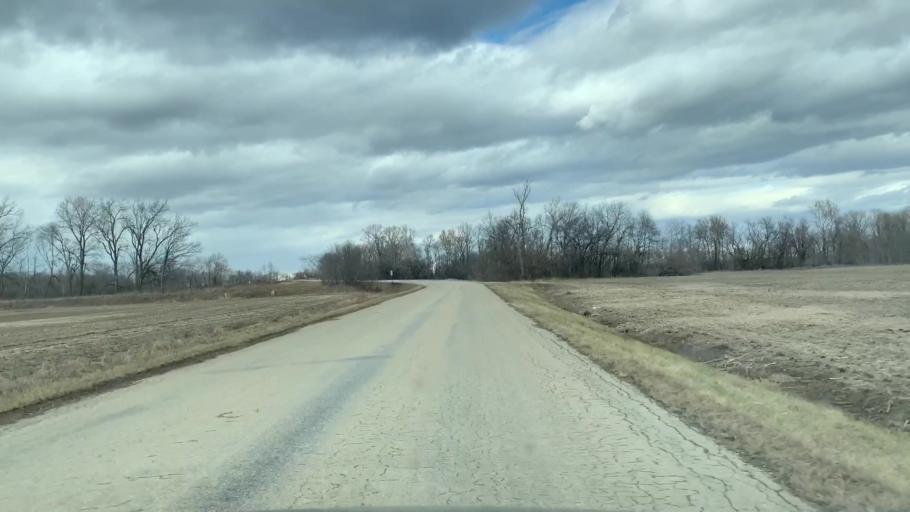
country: US
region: Kansas
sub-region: Allen County
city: Humboldt
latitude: 37.8010
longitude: -95.4705
